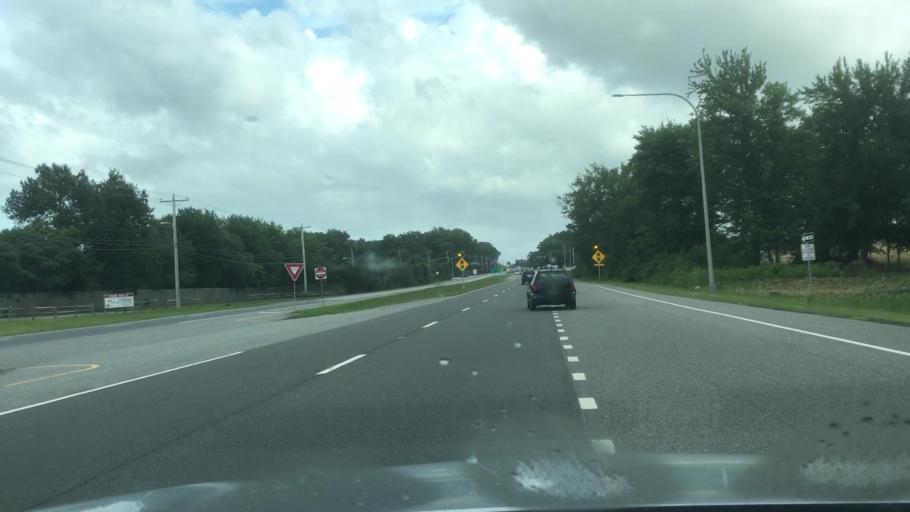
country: US
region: Delaware
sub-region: Kent County
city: Smyrna
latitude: 39.3282
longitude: -75.6239
